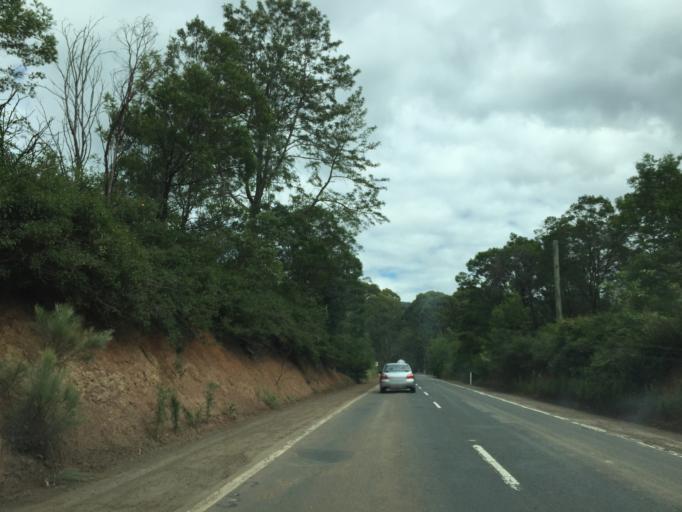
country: AU
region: New South Wales
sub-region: Hawkesbury
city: Richmond
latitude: -33.5485
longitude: 150.6694
